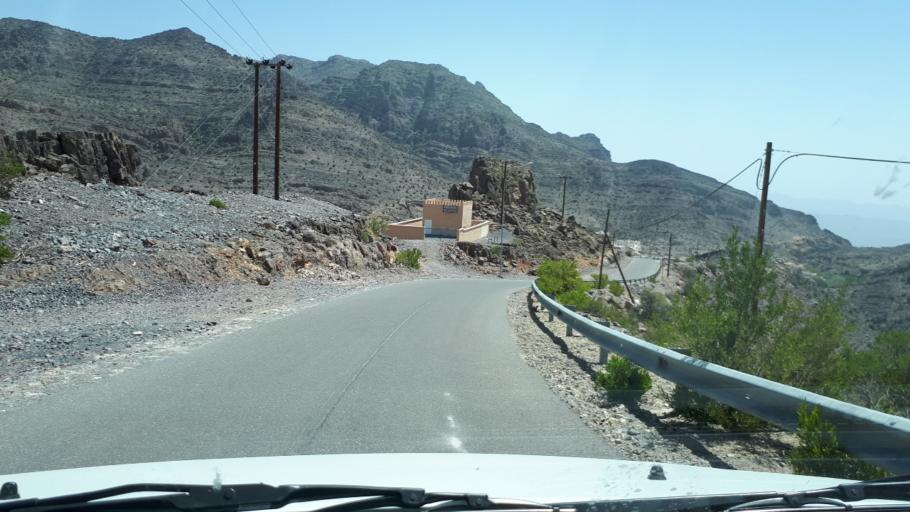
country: OM
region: Muhafazat ad Dakhiliyah
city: Izki
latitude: 23.0900
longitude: 57.7246
